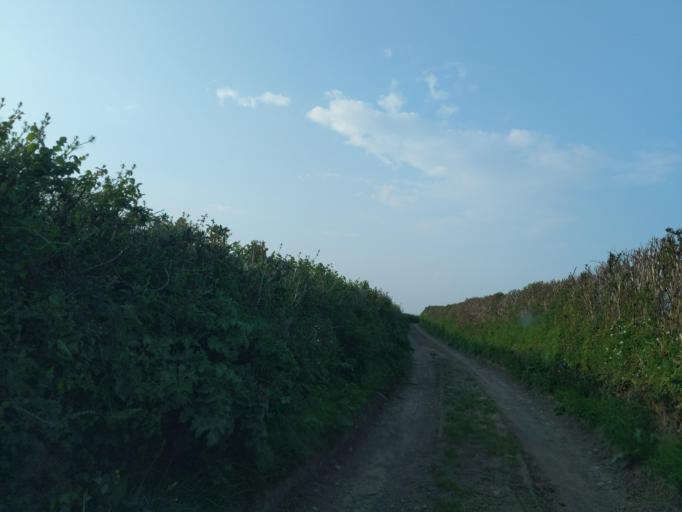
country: GB
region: England
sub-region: Devon
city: Yealmpton
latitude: 50.3552
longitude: -4.0387
